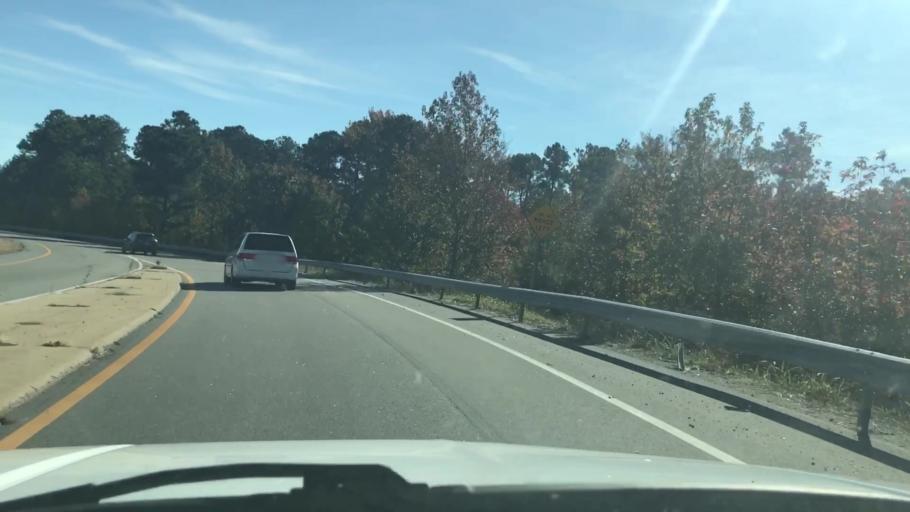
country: US
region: Virginia
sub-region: Henrico County
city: Short Pump
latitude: 37.6468
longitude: -77.5947
